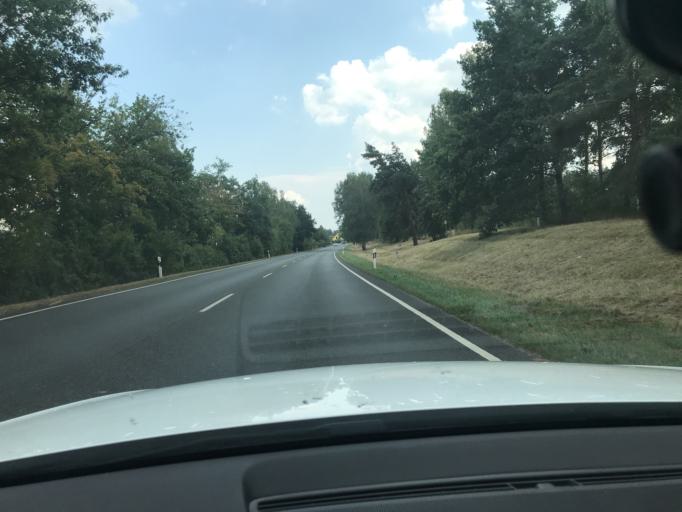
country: DE
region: Bavaria
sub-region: Upper Palatinate
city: Grafenwohr
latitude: 49.7124
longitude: 11.9214
